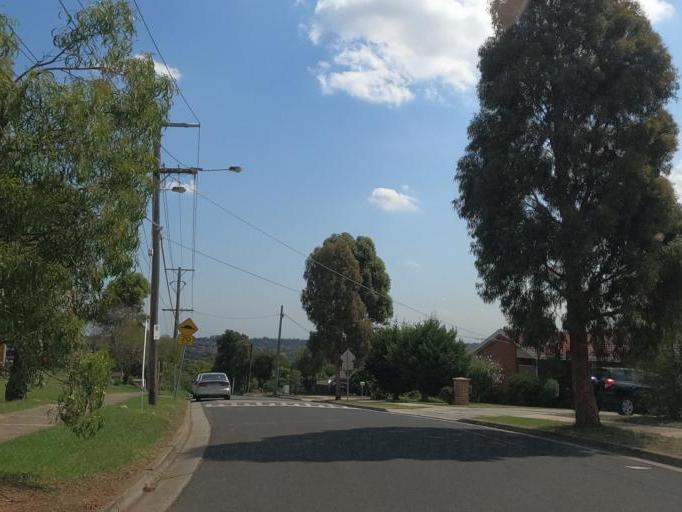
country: AU
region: Victoria
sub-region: Hume
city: Broadmeadows
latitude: -37.6766
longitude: 144.9155
